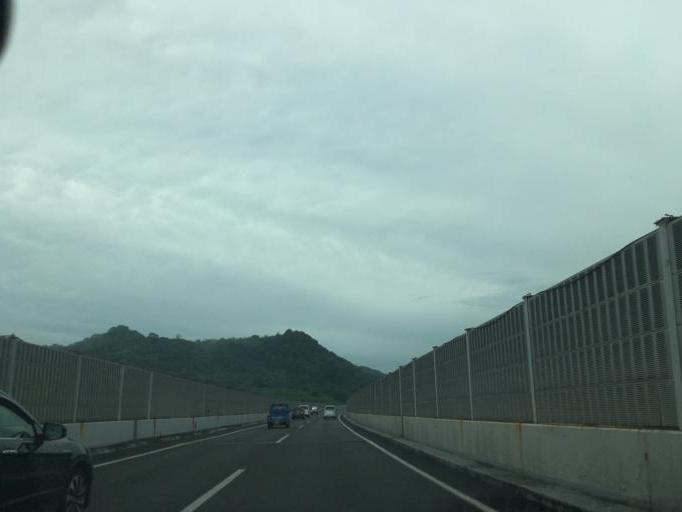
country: JP
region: Saga Prefecture
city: Kanzakimachi-kanzaki
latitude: 33.3392
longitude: 130.3519
